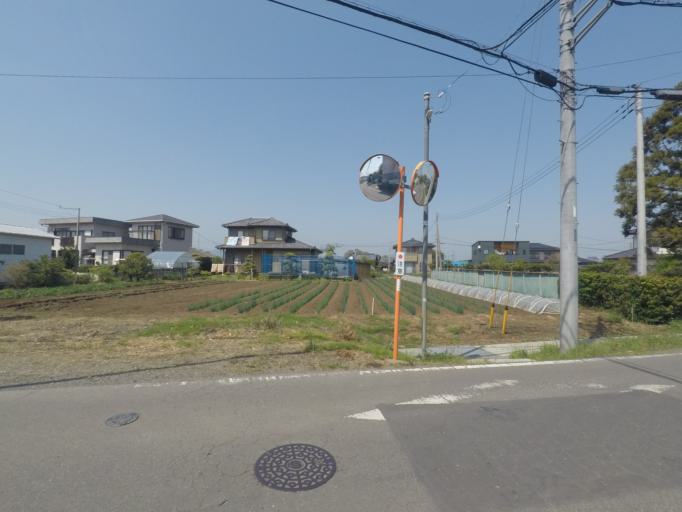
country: JP
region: Ibaraki
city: Naka
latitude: 36.0931
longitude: 140.1441
